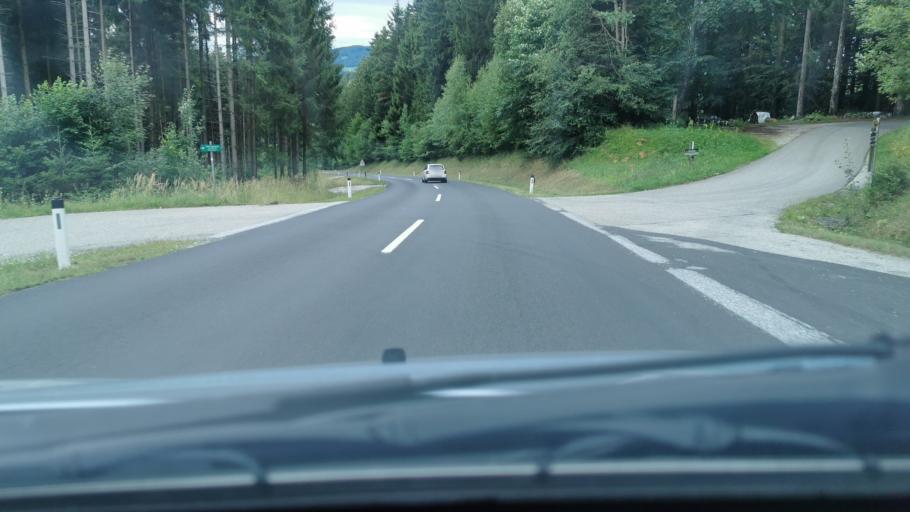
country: AT
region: Styria
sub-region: Politischer Bezirk Weiz
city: Birkfeld
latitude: 47.3641
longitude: 15.6862
